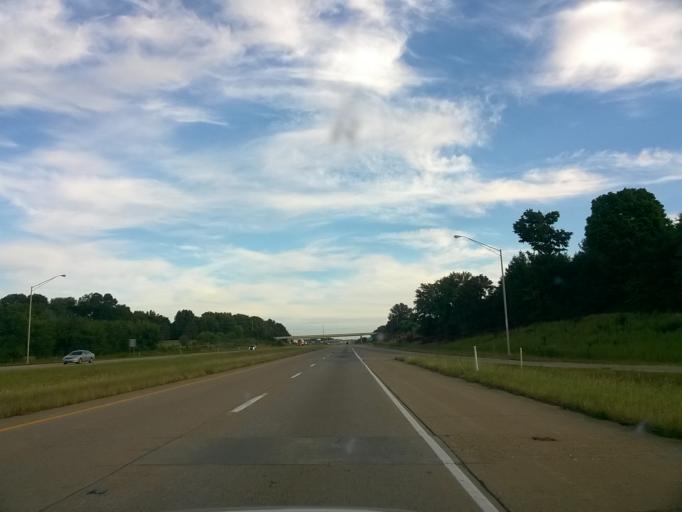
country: US
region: Indiana
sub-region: Vanderburgh County
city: Melody Hill
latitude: 38.0017
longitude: -87.4668
